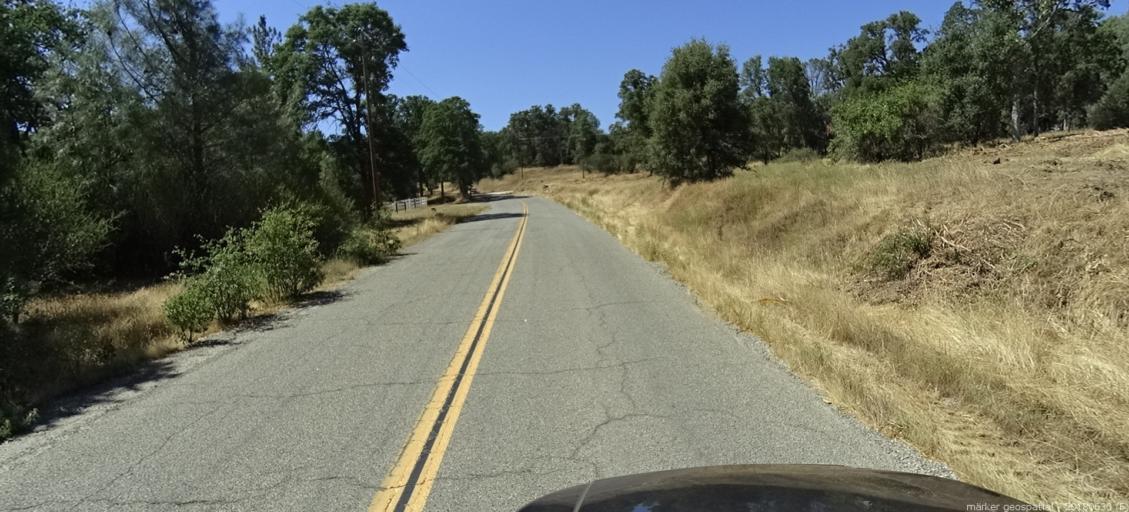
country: US
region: California
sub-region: Fresno County
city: Auberry
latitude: 37.2115
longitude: -119.5024
